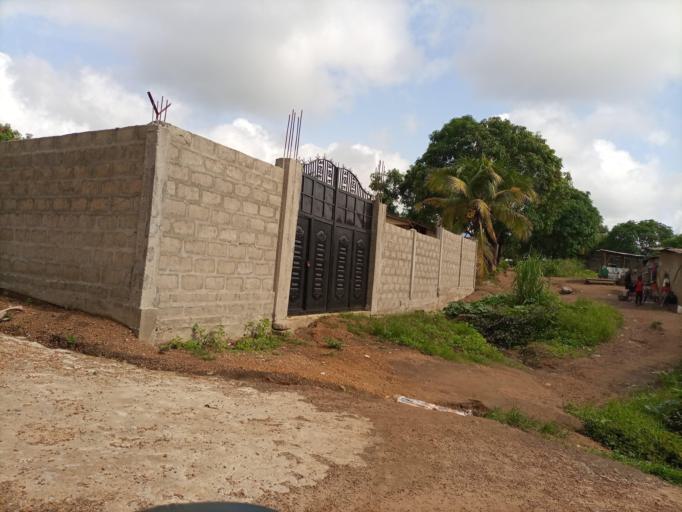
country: SL
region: Southern Province
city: Bo
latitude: 7.9672
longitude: -11.7616
